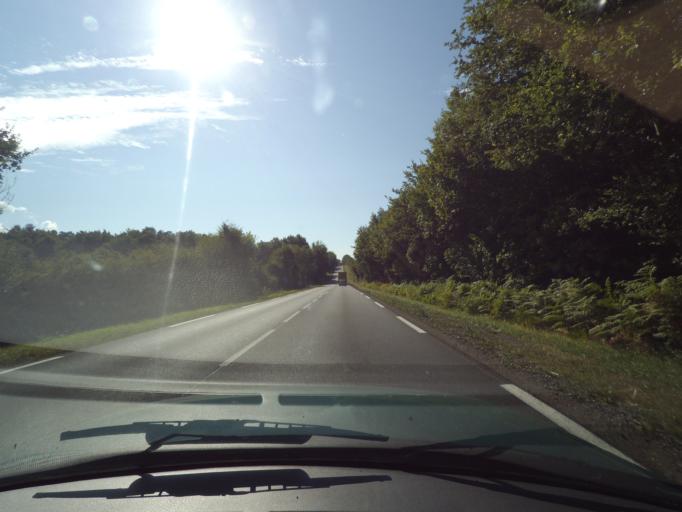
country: FR
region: Poitou-Charentes
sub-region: Departement de la Vienne
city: Terce
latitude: 46.4516
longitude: 0.5665
